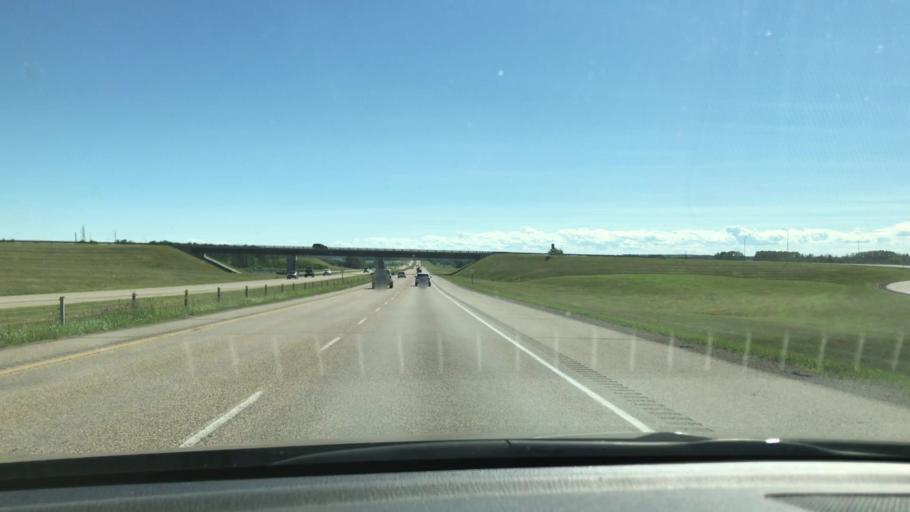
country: CA
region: Alberta
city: Penhold
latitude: 52.0046
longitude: -113.9595
